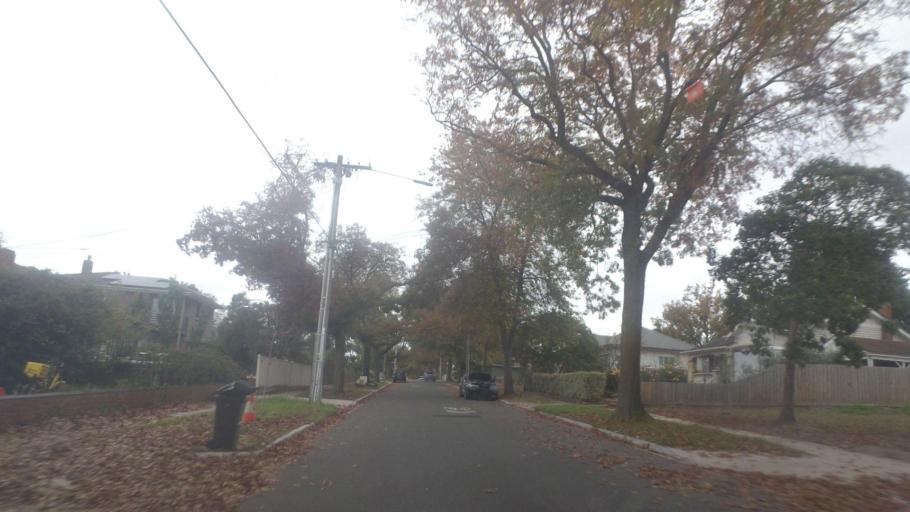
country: AU
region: Victoria
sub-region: Whitehorse
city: Box Hill South
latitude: -37.8304
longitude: 145.1271
